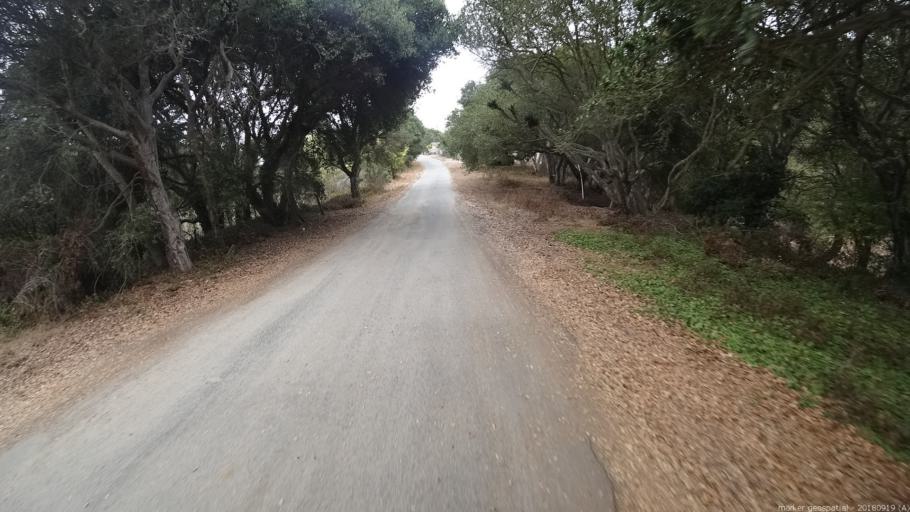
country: US
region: California
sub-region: Monterey County
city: Elkhorn
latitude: 36.8042
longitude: -121.7291
